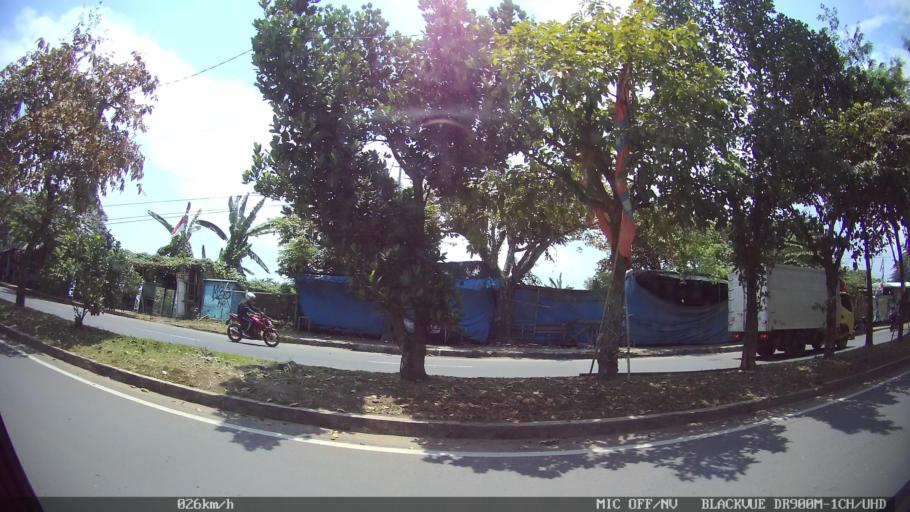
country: ID
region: Lampung
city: Kedaton
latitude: -5.3828
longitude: 105.2796
